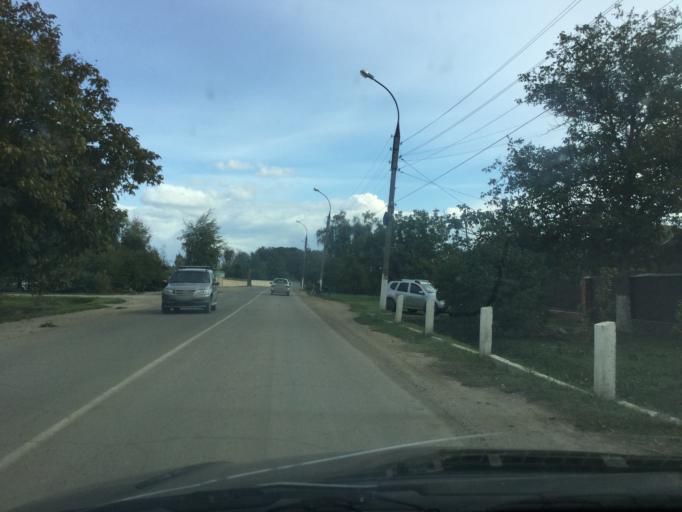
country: RU
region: Krasnodarskiy
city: Sovkhoznyy
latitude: 45.2850
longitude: 38.1044
